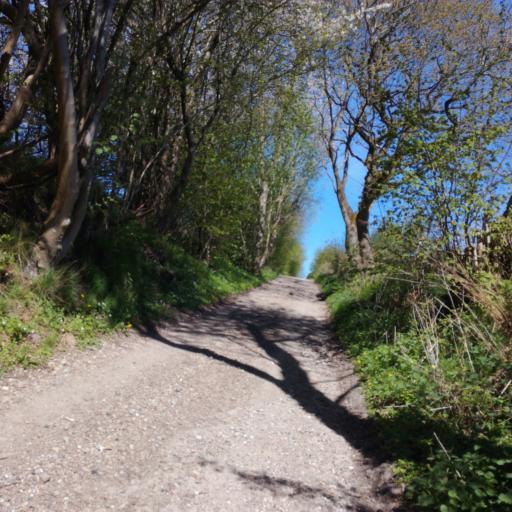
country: DK
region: South Denmark
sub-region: Vejle Kommune
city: Borkop
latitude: 55.6120
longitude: 9.6857
